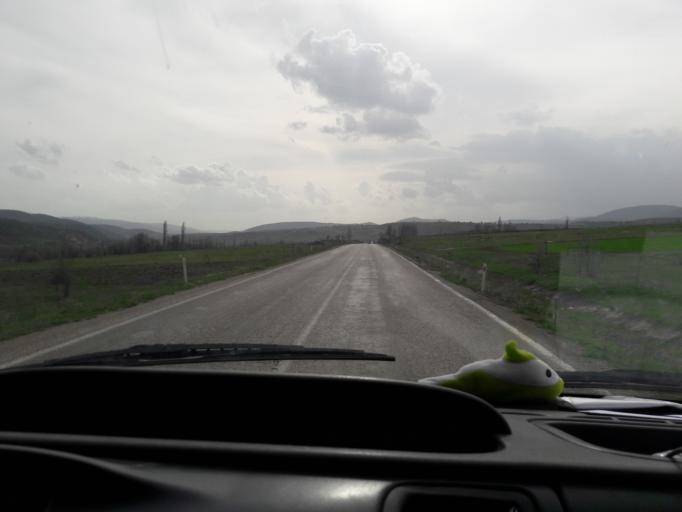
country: TR
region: Gumushane
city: Siran
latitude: 40.1616
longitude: 39.0308
